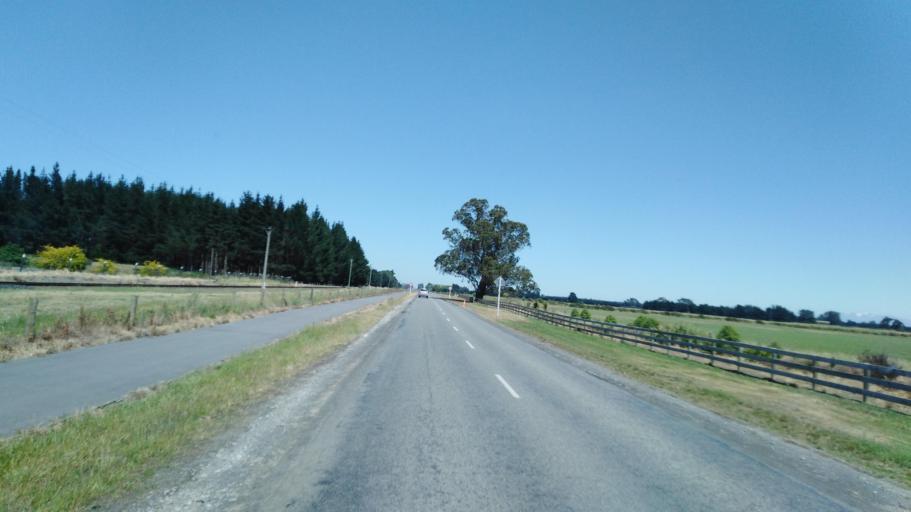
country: NZ
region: Canterbury
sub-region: Selwyn District
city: Prebbleton
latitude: -43.5606
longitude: 172.4569
